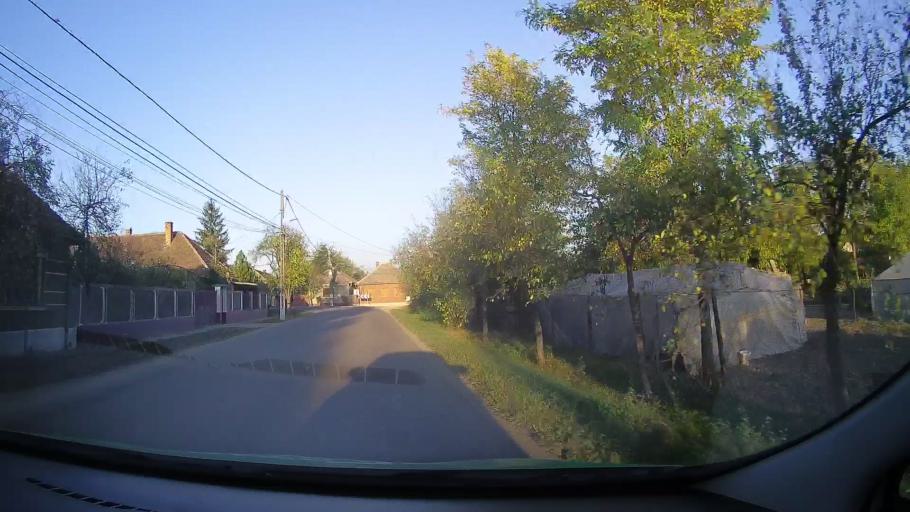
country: RO
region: Bihor
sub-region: Comuna Salard
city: Salard
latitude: 47.2288
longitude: 22.0309
